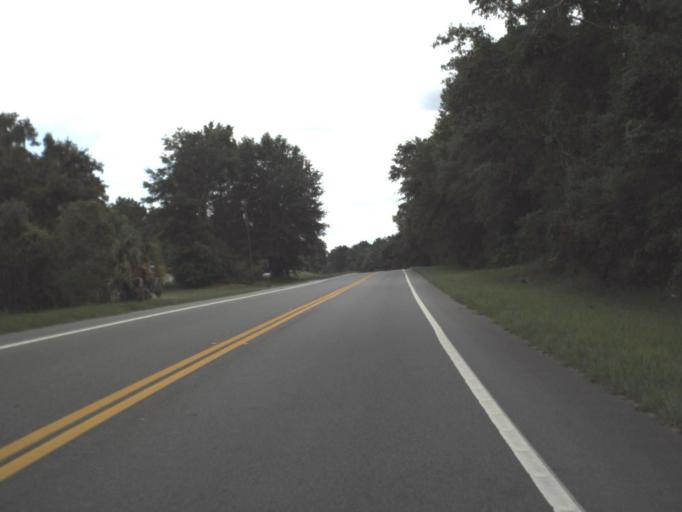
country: US
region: Florida
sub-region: Madison County
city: Madison
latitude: 30.6091
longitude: -83.3452
